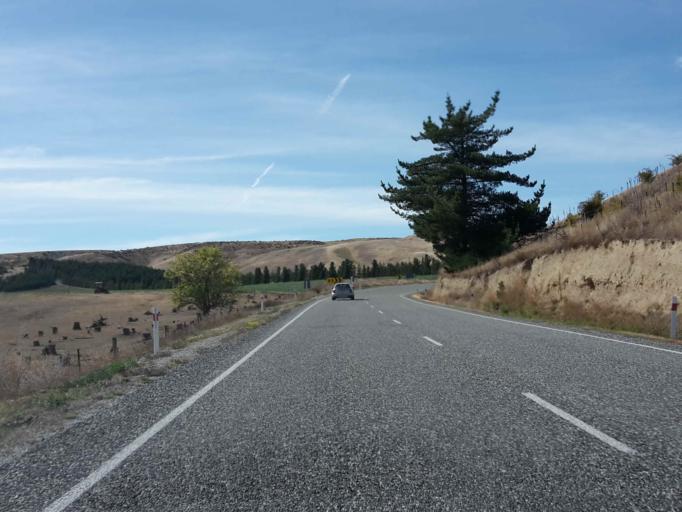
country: NZ
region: Otago
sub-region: Queenstown-Lakes District
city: Wanaka
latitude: -44.8025
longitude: 169.4707
